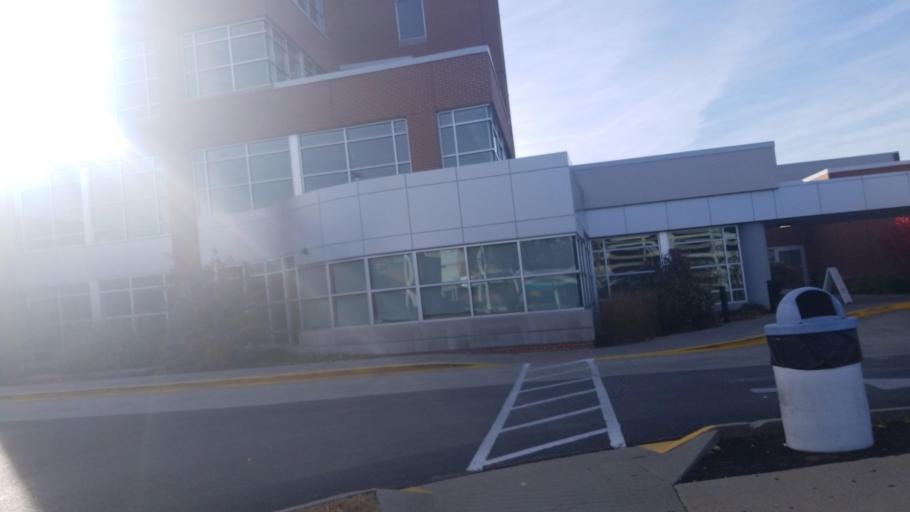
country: US
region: Illinois
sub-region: Jackson County
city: Carbondale
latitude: 37.7279
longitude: -89.2207
